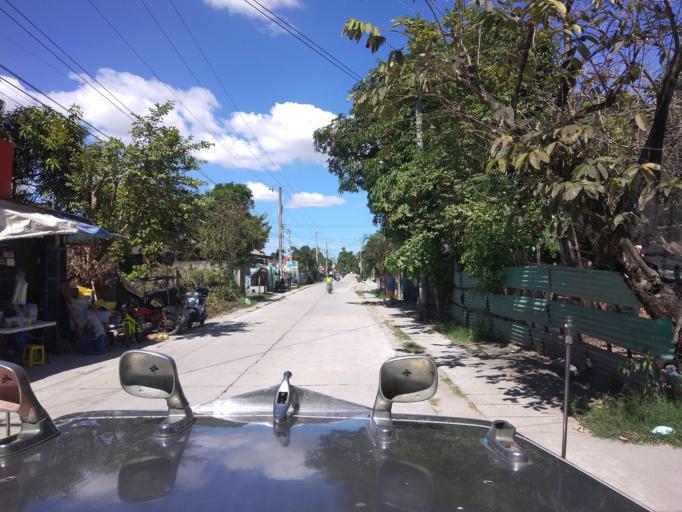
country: PH
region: Central Luzon
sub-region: Province of Pampanga
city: Magliman
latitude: 15.0390
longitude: 120.6457
